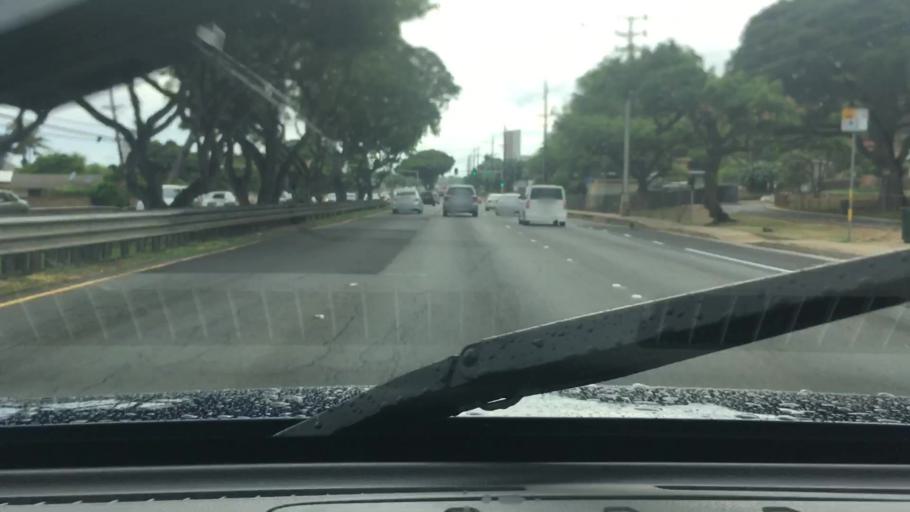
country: US
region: Hawaii
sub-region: Honolulu County
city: Waimanalo
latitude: 21.2774
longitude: -157.7747
